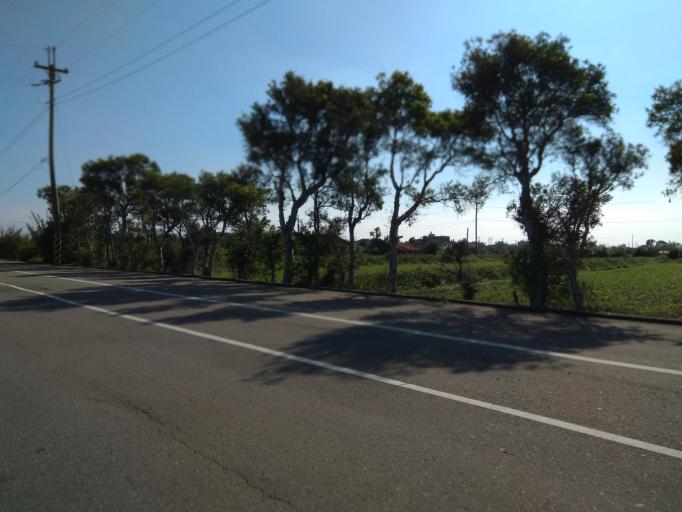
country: TW
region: Taiwan
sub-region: Hsinchu
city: Zhubei
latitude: 25.0247
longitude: 121.0811
